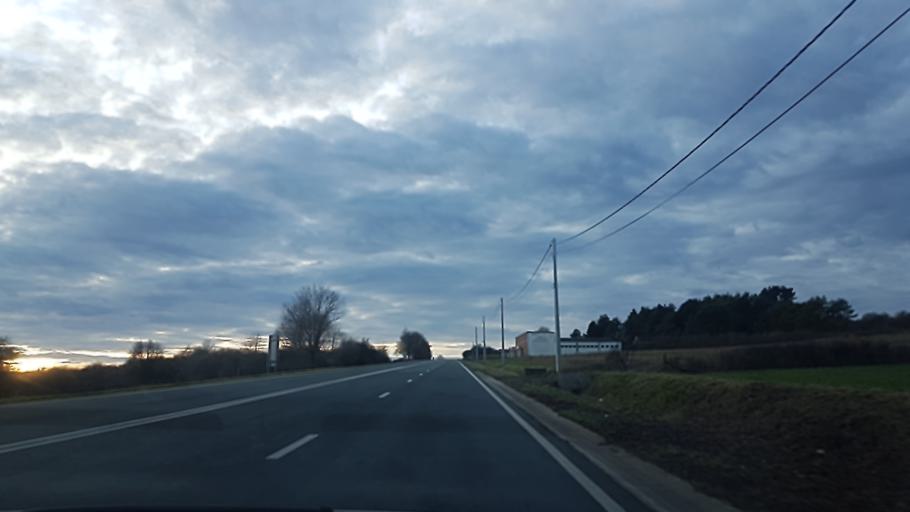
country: BE
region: Wallonia
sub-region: Province de Namur
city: Couvin
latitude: 50.0478
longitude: 4.4448
